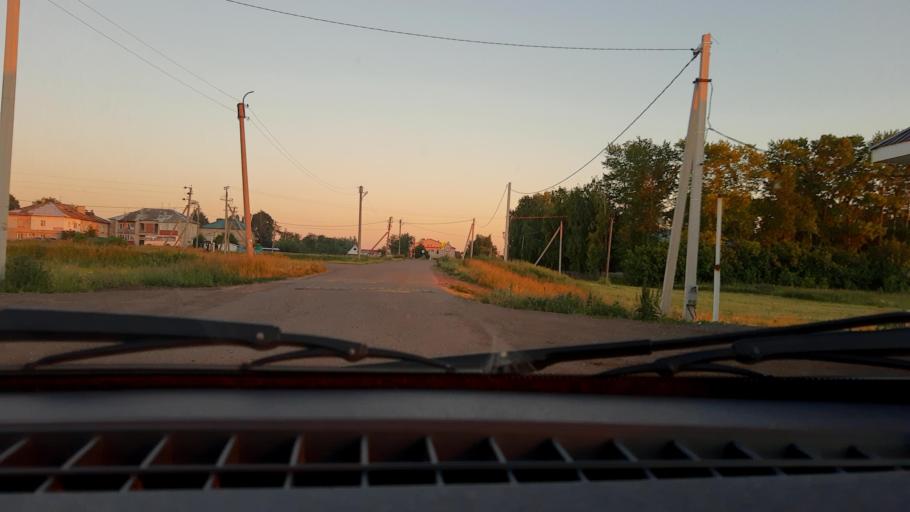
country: RU
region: Bashkortostan
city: Asanovo
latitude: 54.8911
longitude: 55.6244
